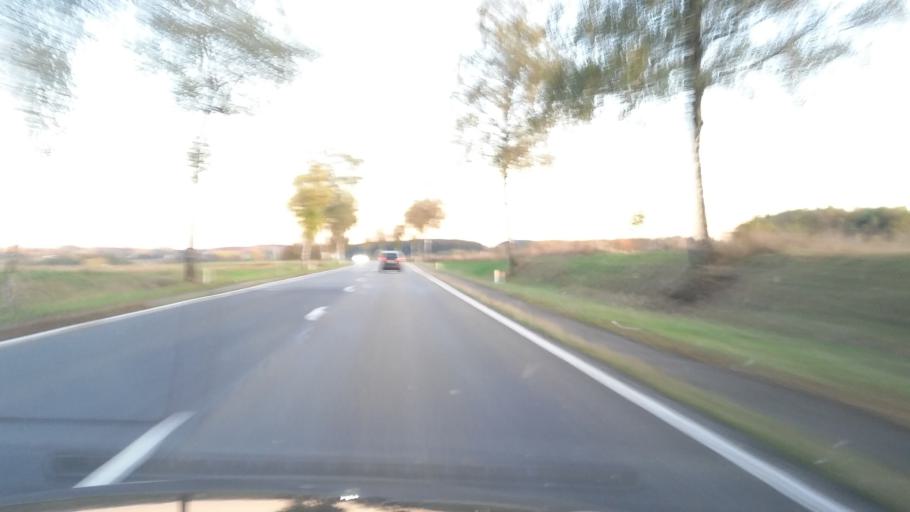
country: BE
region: Wallonia
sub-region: Province du Luxembourg
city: Florenville
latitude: 49.6924
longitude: 5.3326
